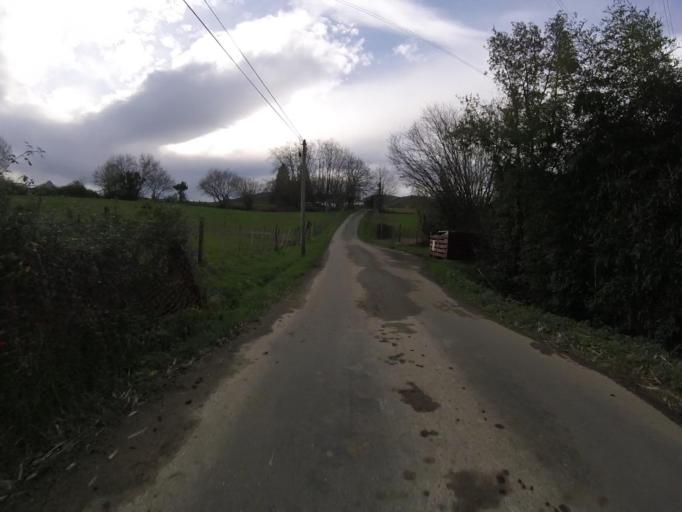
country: FR
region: Aquitaine
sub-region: Departement des Pyrenees-Atlantiques
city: Urrugne
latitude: 43.3413
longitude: -1.6989
